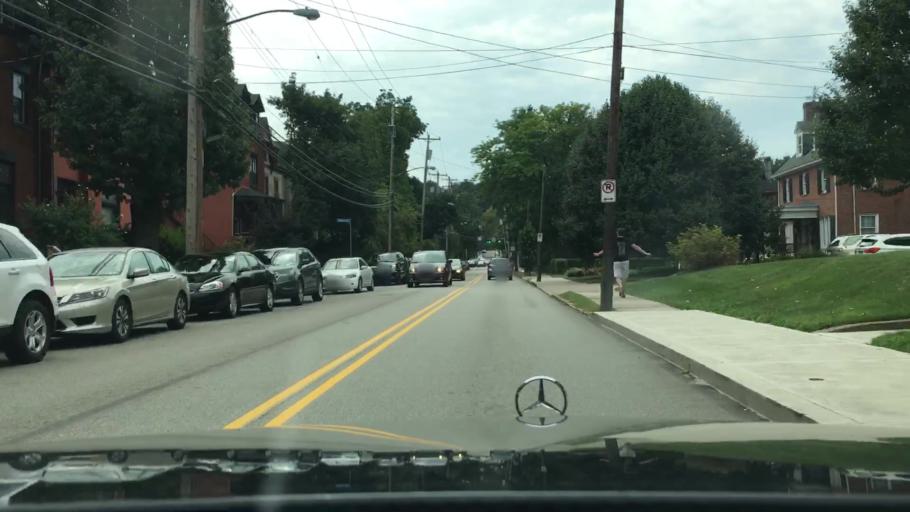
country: US
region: Pennsylvania
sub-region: Allegheny County
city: Bloomfield
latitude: 40.4522
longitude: -79.9364
